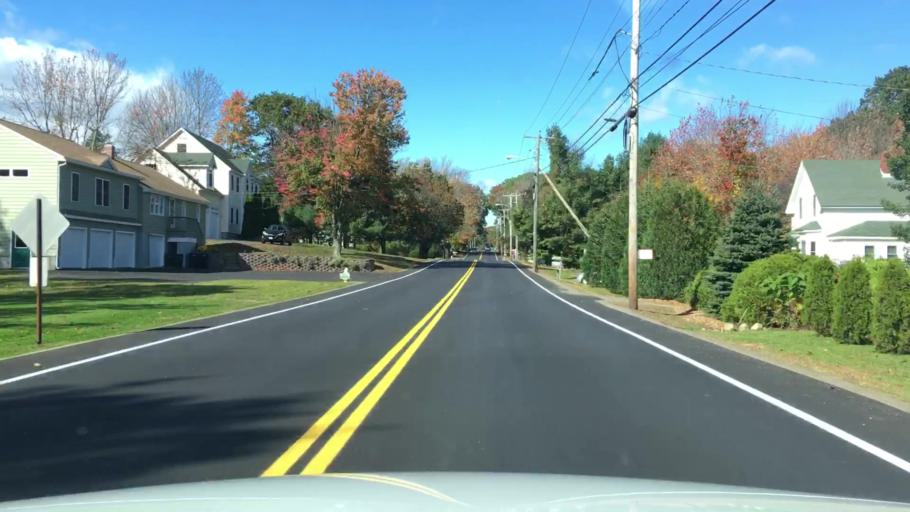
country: US
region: Maine
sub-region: York County
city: Biddeford
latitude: 43.4566
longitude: -70.4308
